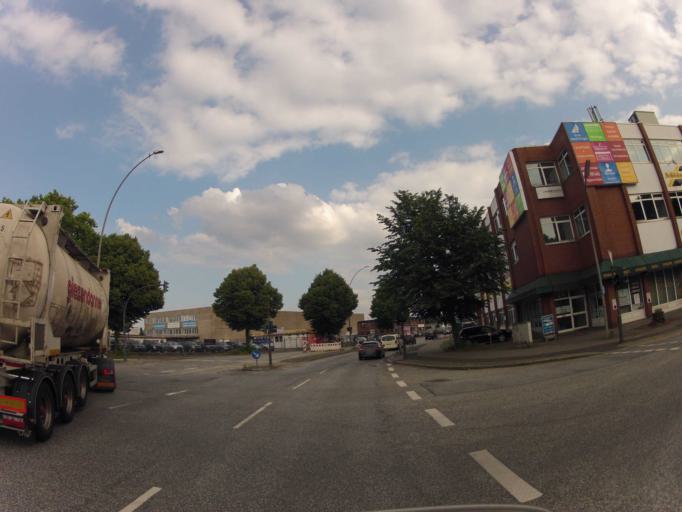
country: DE
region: Hamburg
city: Hammerbrook
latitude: 53.5464
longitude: 10.0397
